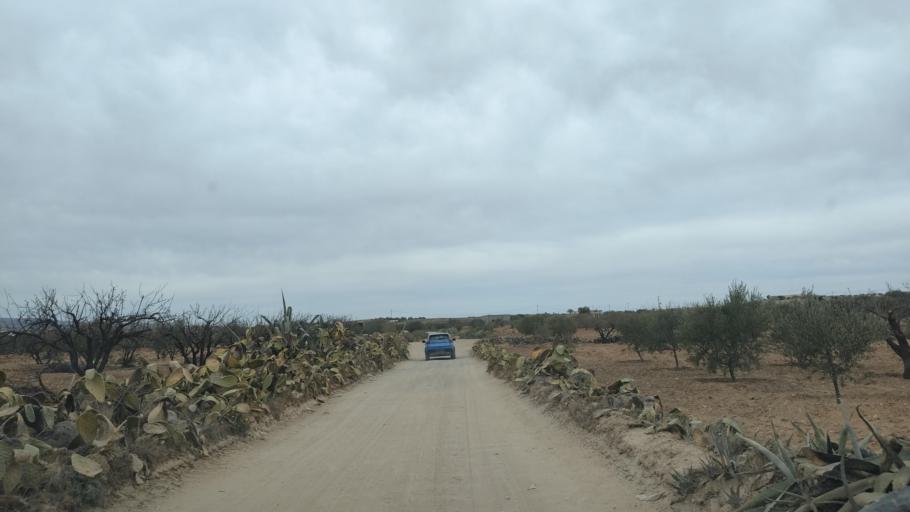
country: TN
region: Al Qasrayn
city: Kasserine
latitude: 35.2316
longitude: 8.9103
